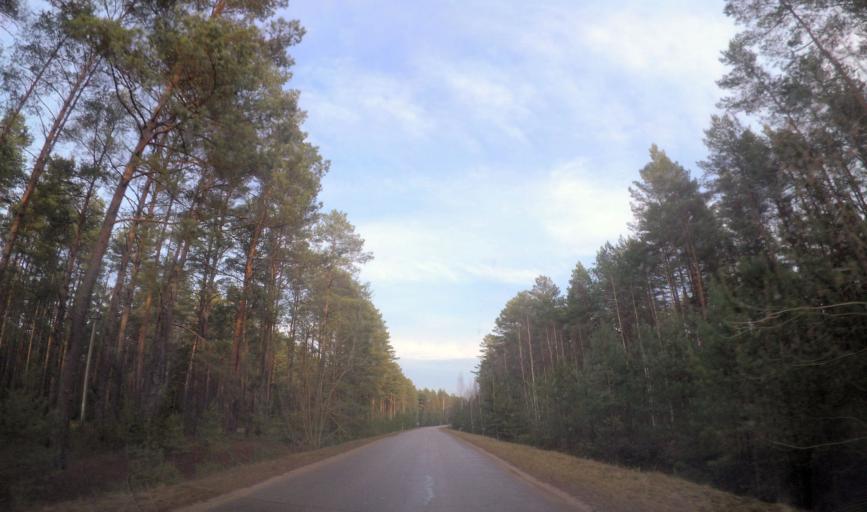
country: LT
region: Alytaus apskritis
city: Druskininkai
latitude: 53.8964
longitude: 24.1409
